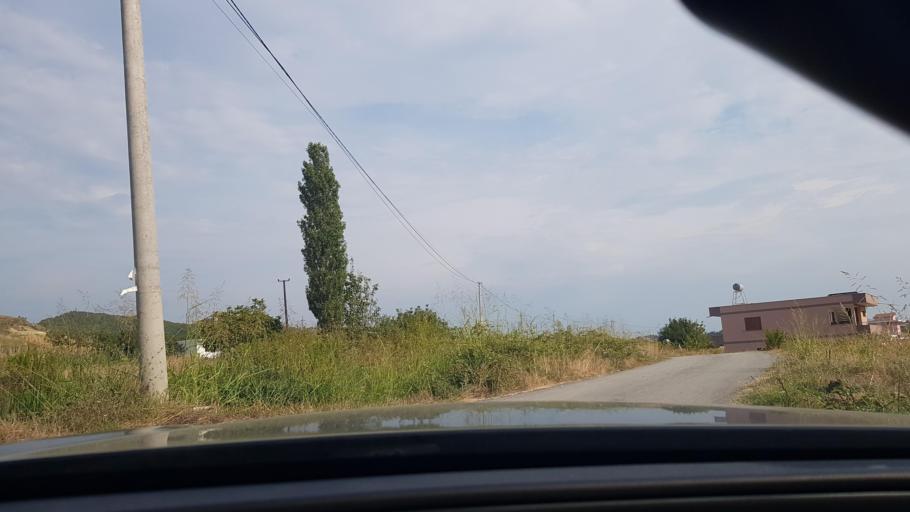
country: AL
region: Durres
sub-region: Rrethi i Durresit
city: Manze
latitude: 41.4736
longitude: 19.5661
